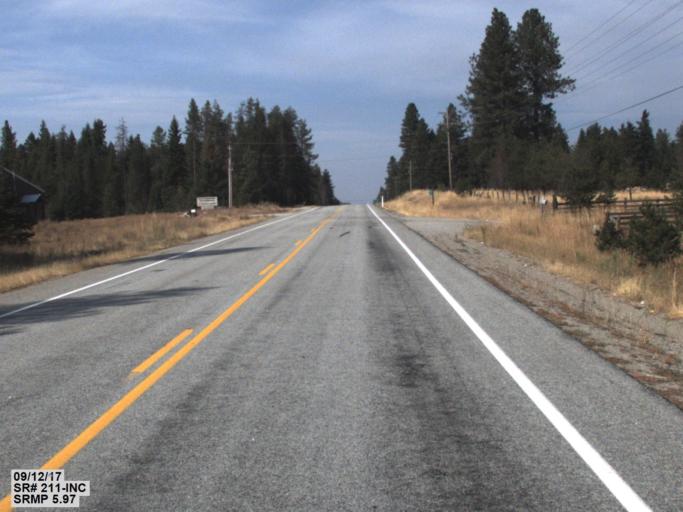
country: US
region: Washington
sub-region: Pend Oreille County
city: Newport
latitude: 48.1756
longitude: -117.3015
